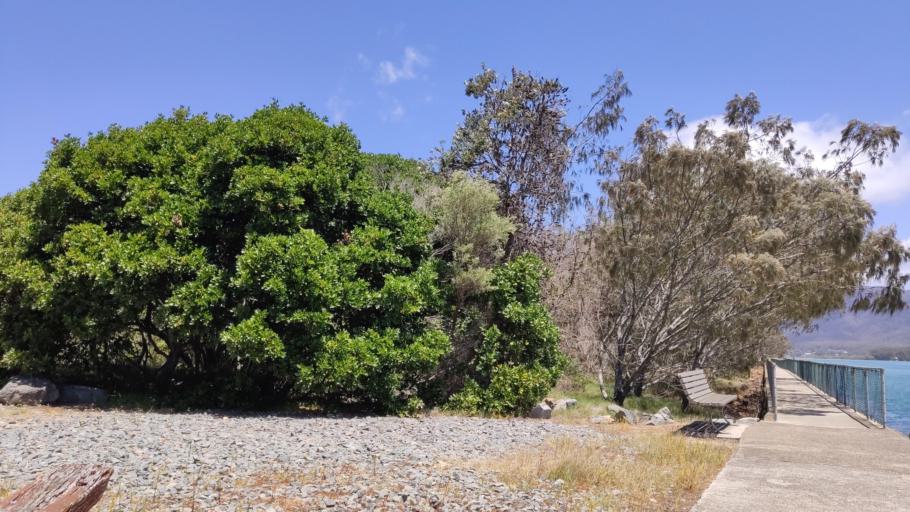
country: AU
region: New South Wales
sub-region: Port Macquarie-Hastings
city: North Haven
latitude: -31.6388
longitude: 152.8298
